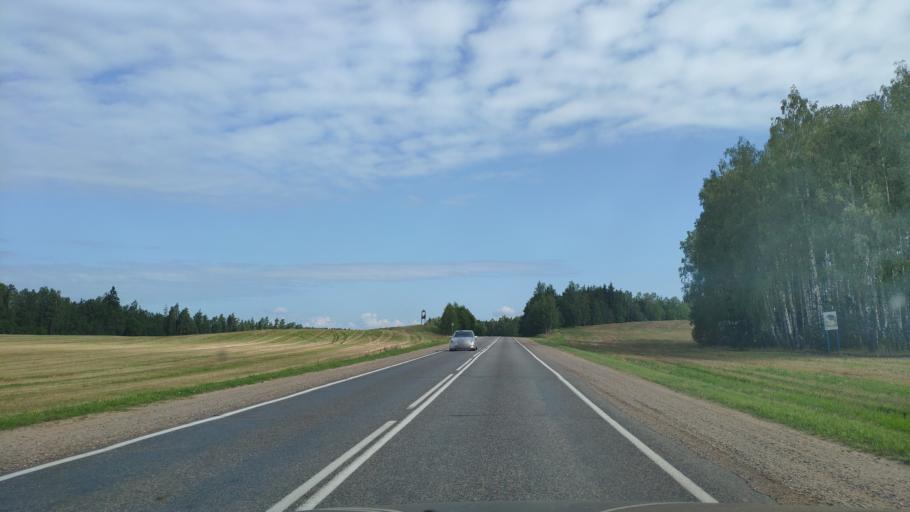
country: BY
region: Minsk
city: Zaslawye
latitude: 53.9613
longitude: 27.2450
